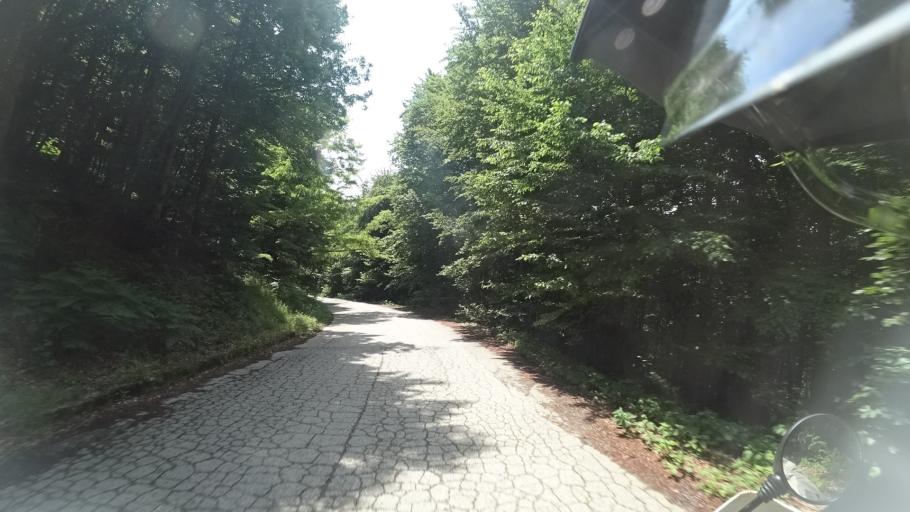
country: HR
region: Sisacko-Moslavacka
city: Gvozd
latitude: 45.3121
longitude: 15.8049
